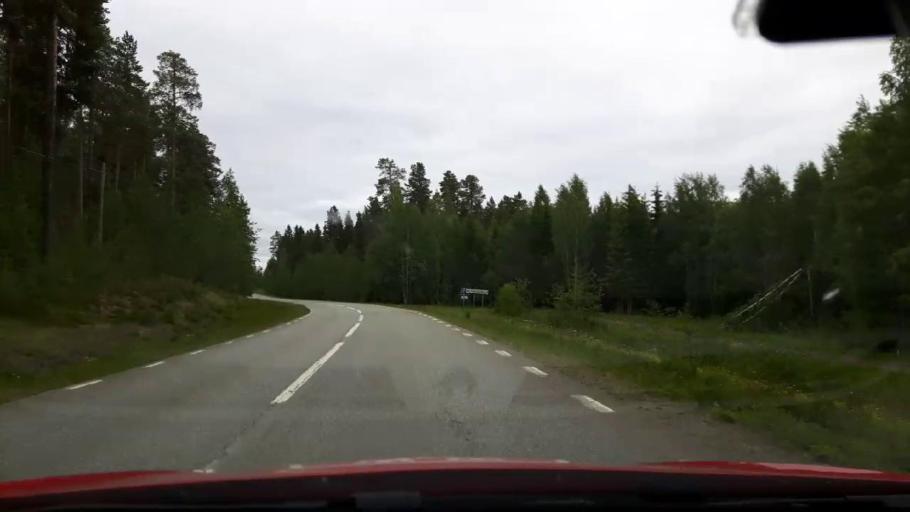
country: SE
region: Jaemtland
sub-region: Stroemsunds Kommun
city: Stroemsund
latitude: 63.3887
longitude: 15.6759
